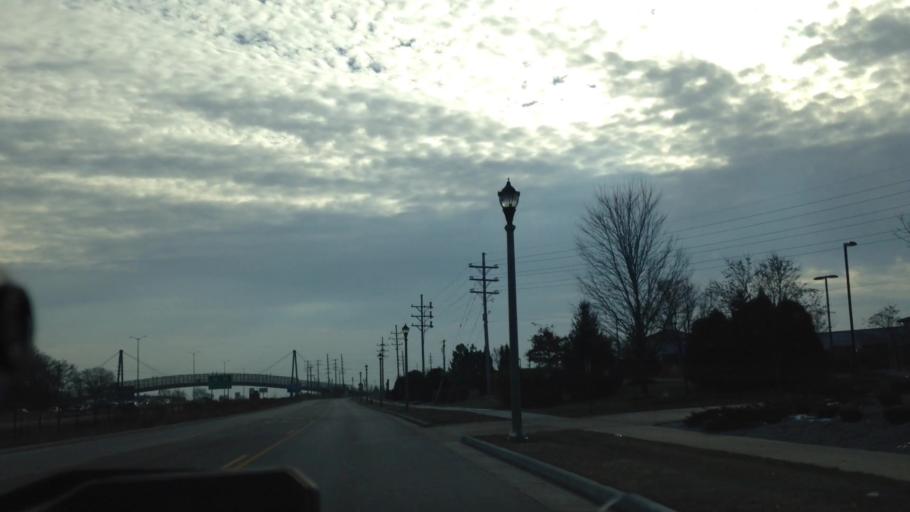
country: US
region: Wisconsin
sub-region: Waukesha County
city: Menomonee Falls
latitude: 43.1890
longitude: -88.1173
